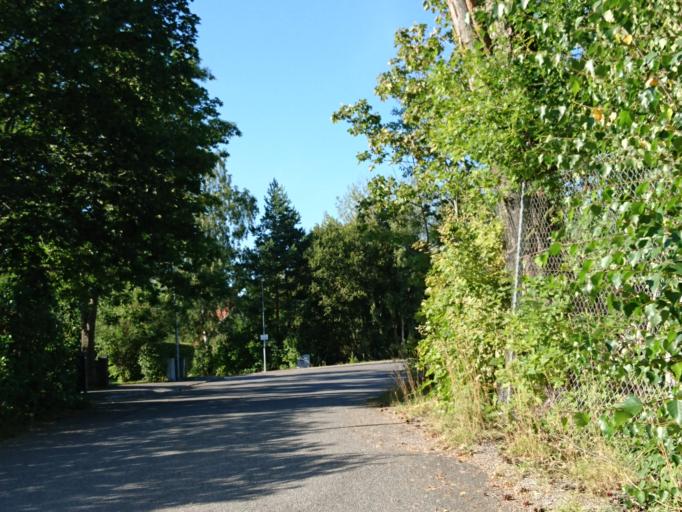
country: SE
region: Stockholm
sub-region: Huddinge Kommun
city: Segeltorp
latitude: 59.2754
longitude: 17.9468
